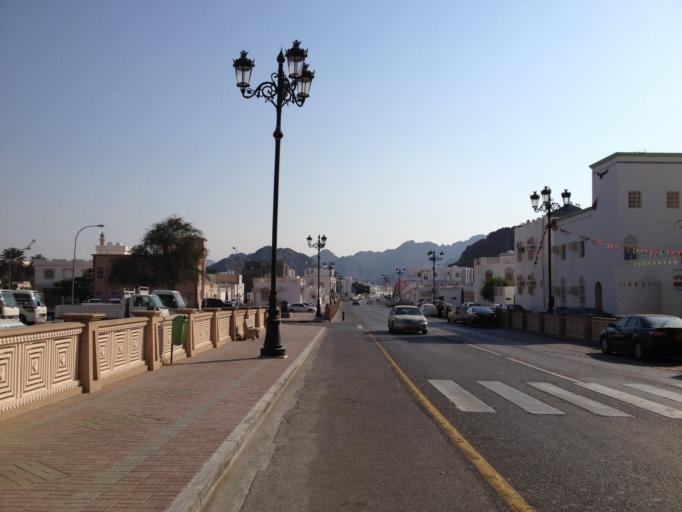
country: OM
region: Muhafazat Masqat
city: Muscat
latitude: 23.6047
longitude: 58.5974
